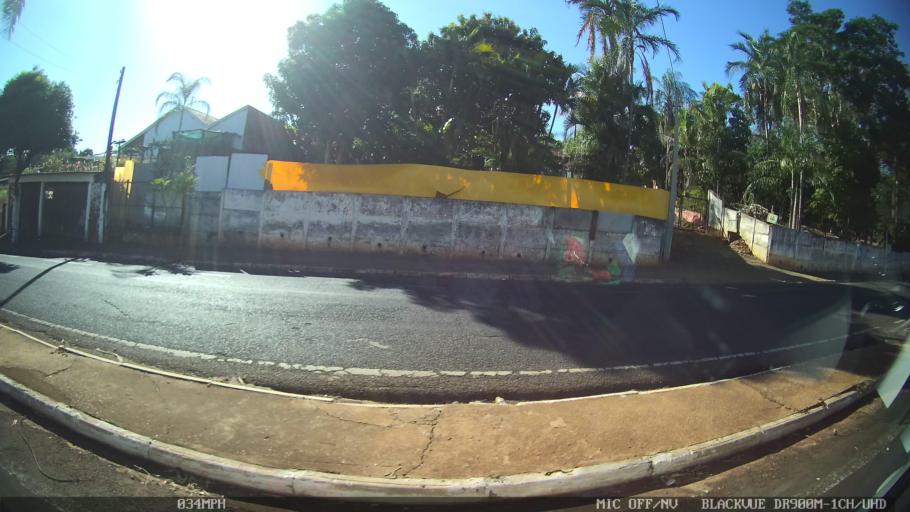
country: BR
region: Sao Paulo
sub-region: Olimpia
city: Olimpia
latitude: -20.7431
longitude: -48.8996
